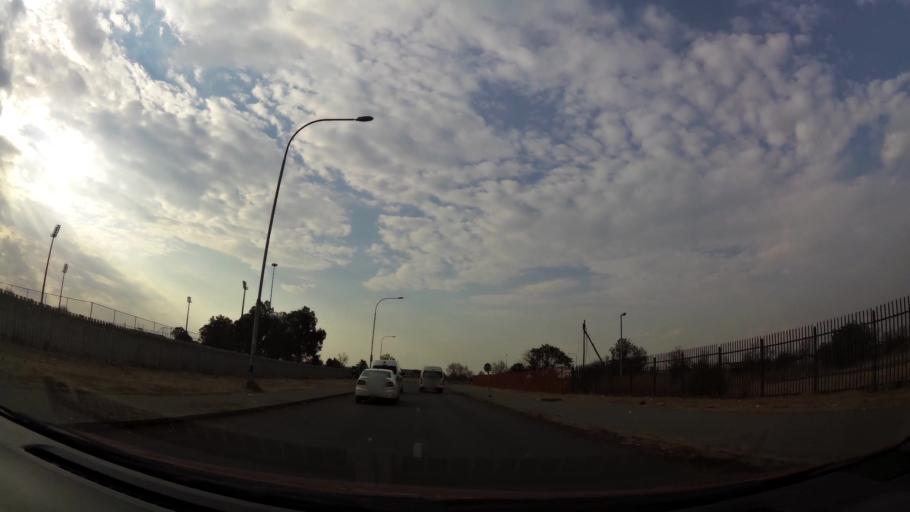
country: ZA
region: Gauteng
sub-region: Sedibeng District Municipality
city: Vanderbijlpark
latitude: -26.6894
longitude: 27.8677
